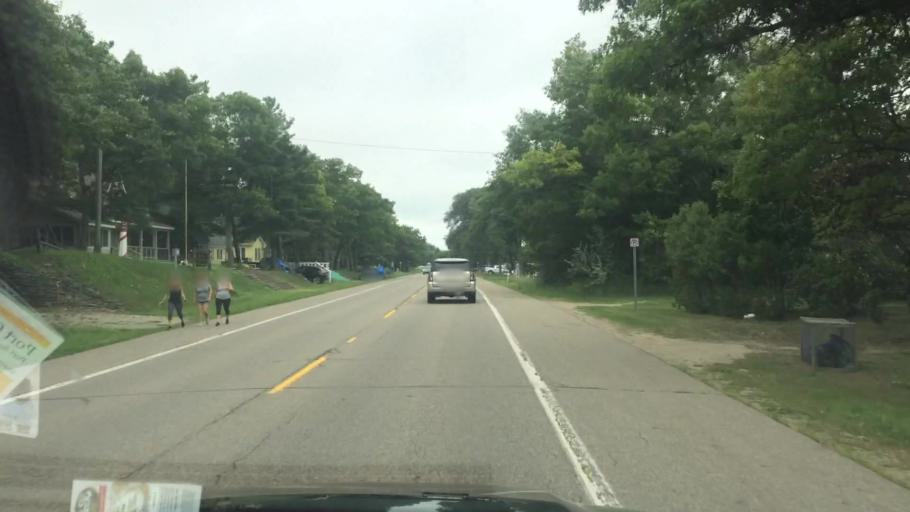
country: US
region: Michigan
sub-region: Huron County
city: Pigeon
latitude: 43.9787
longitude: -83.2351
